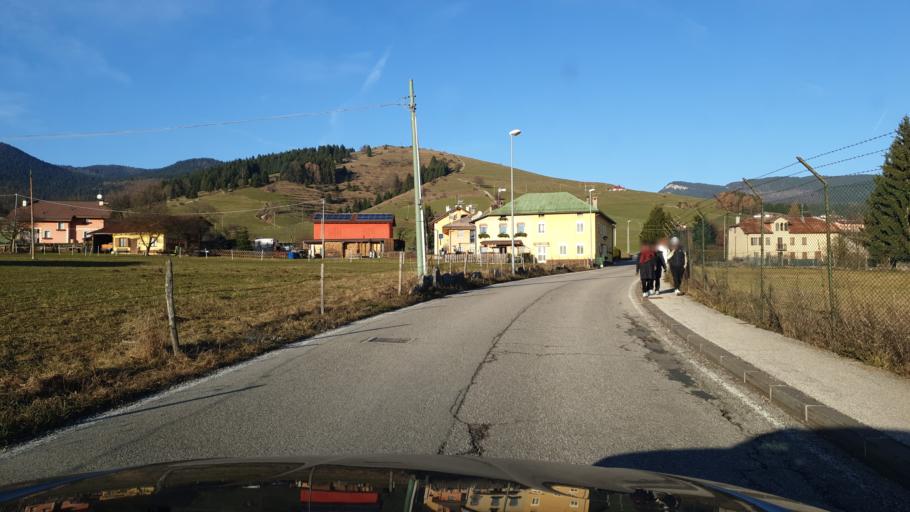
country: IT
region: Veneto
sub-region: Provincia di Vicenza
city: Asiago
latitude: 45.8854
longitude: 11.5082
